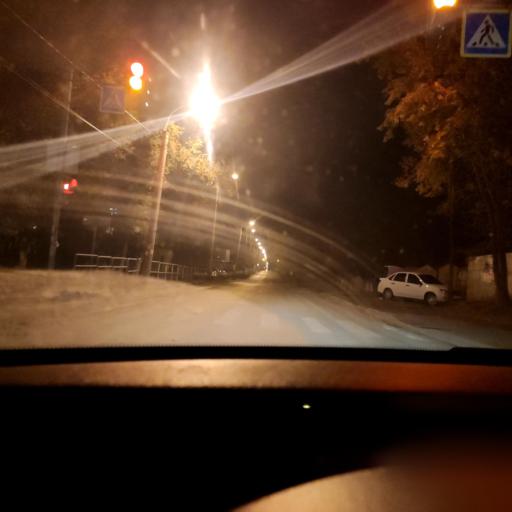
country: RU
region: Samara
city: Samara
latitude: 53.1870
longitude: 50.1795
